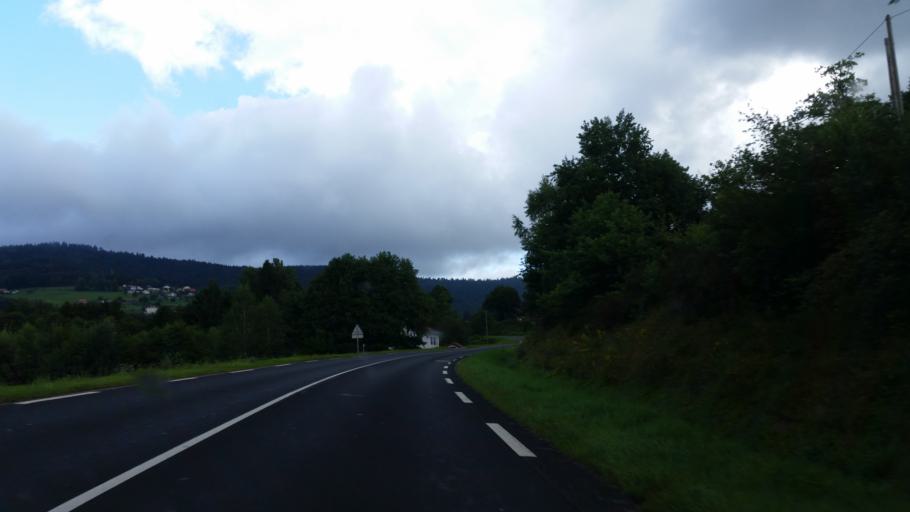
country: FR
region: Lorraine
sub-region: Departement des Vosges
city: Le Syndicat
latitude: 48.0394
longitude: 6.6804
